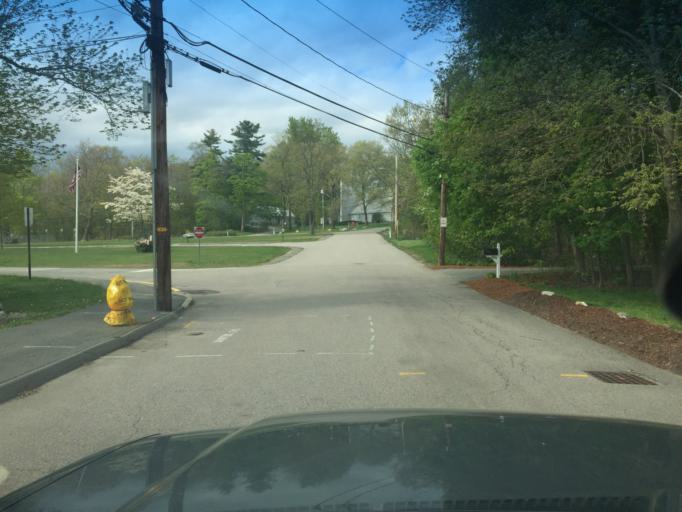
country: US
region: Massachusetts
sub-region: Norfolk County
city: Westwood
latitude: 42.2258
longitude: -71.2188
